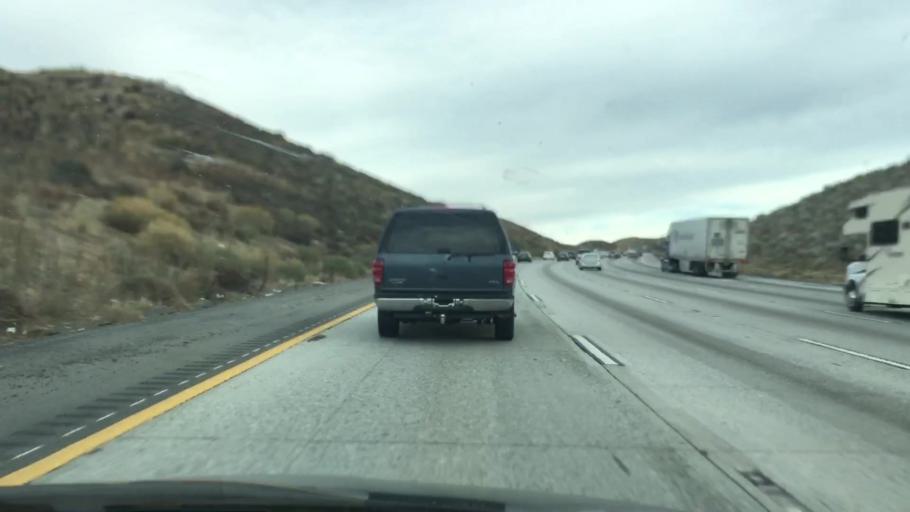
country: US
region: California
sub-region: San Bernardino County
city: Oak Hills
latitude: 34.3404
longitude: -117.4728
